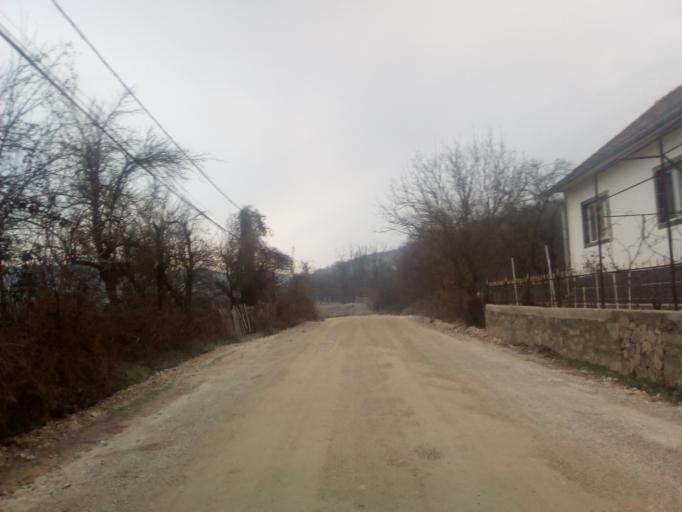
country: RO
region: Mehedinti
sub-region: Comuna Eselnita
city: Eselnita
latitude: 44.6938
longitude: 22.3681
